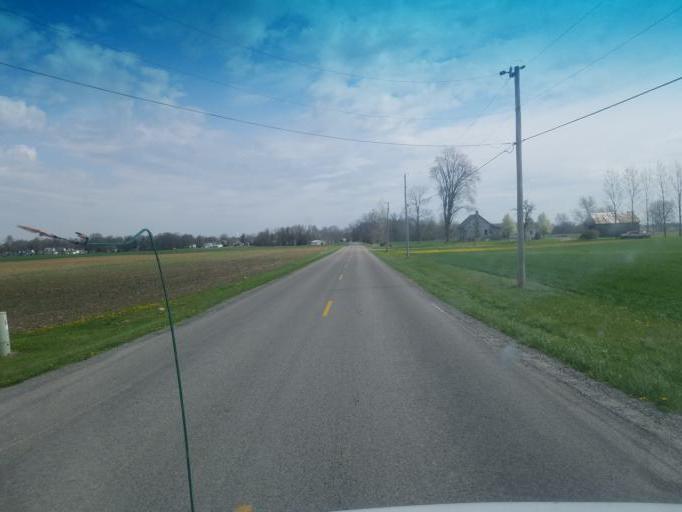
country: US
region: Ohio
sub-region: Logan County
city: Northwood
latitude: 40.4984
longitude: -83.7560
